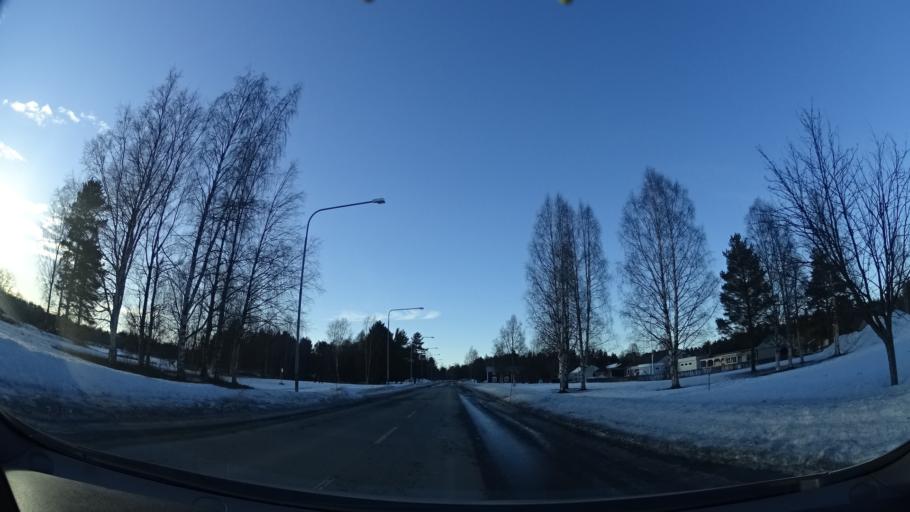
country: SE
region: Vaesterbotten
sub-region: Skelleftea Kommun
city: Byske
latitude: 64.9480
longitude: 21.2256
